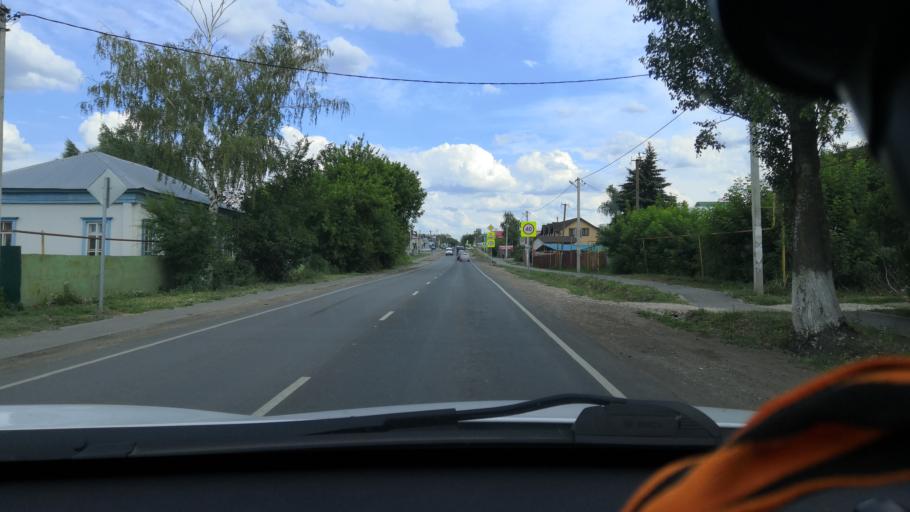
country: RU
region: Samara
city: Novosemeykino
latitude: 53.3782
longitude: 50.3441
